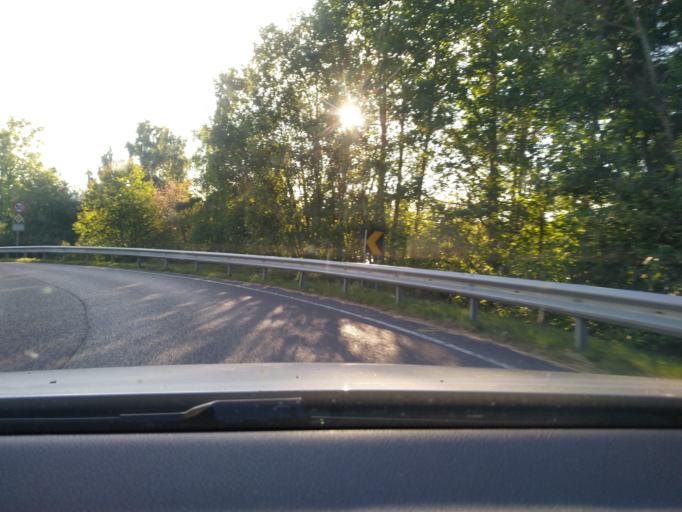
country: NO
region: Akershus
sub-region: Fet
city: Fetsund
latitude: 59.9317
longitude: 11.1830
